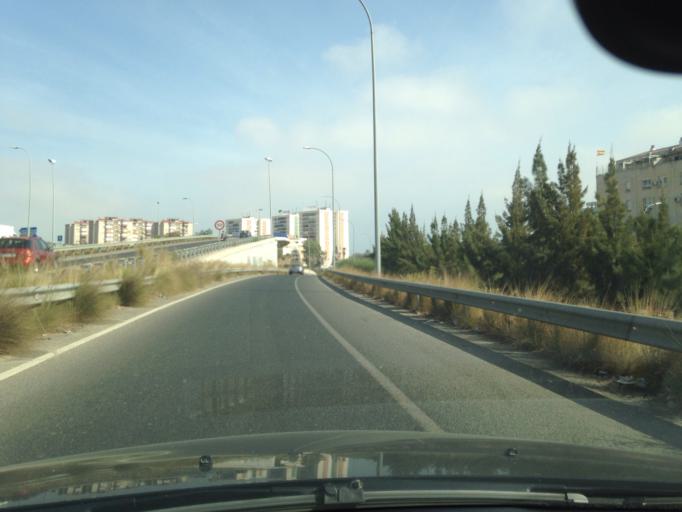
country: ES
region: Andalusia
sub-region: Provincia de Malaga
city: Malaga
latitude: 36.7119
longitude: -4.4615
